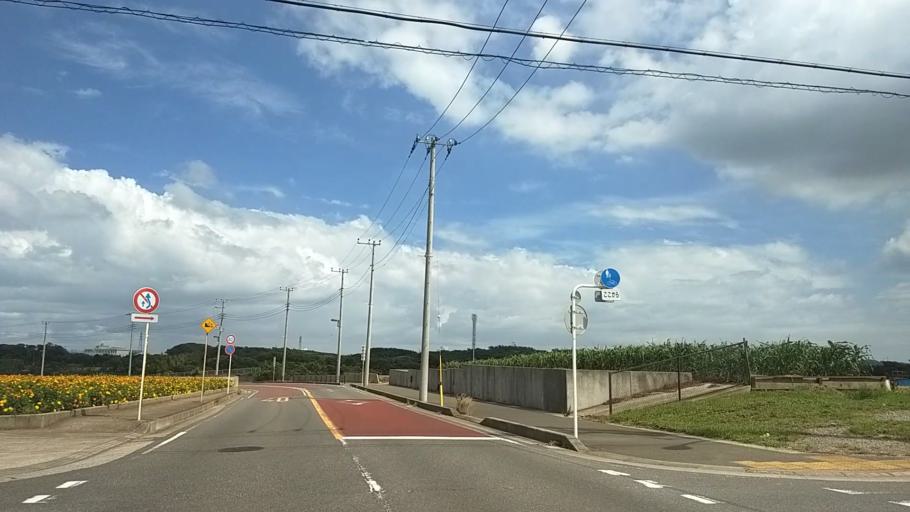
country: JP
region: Kanagawa
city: Miura
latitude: 35.1954
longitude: 139.6150
